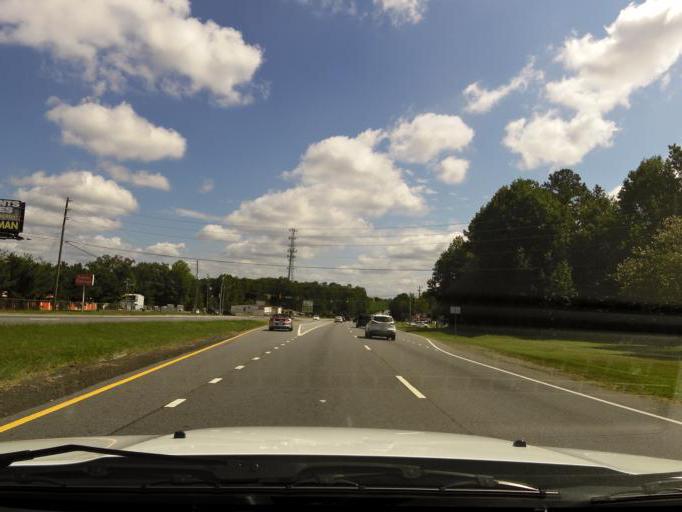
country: US
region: Georgia
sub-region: Cobb County
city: Kennesaw
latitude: 34.0271
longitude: -84.6391
